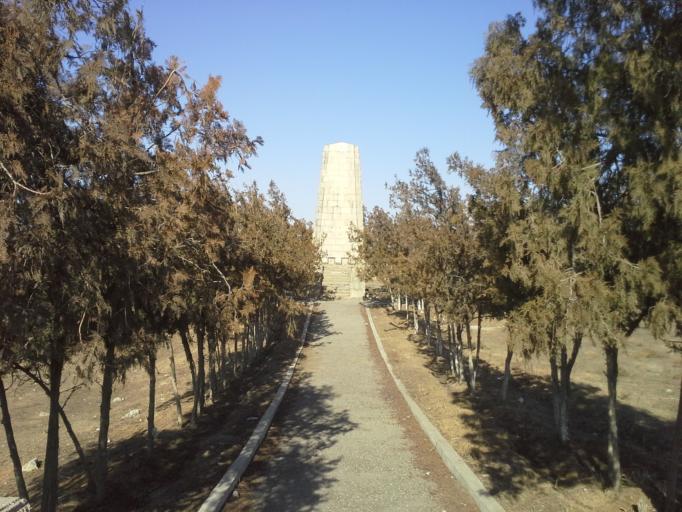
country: TM
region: Ahal
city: Annau
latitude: 37.8963
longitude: 58.6220
